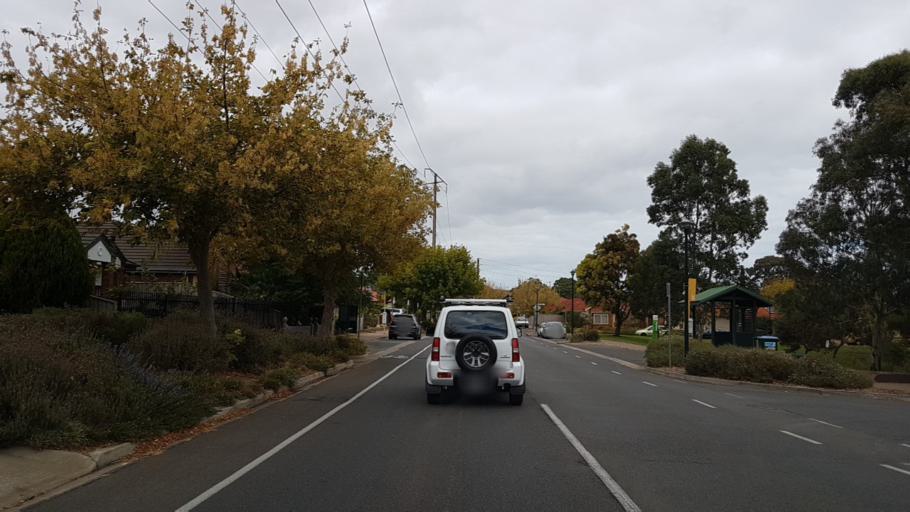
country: AU
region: South Australia
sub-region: Marion
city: Marion
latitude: -35.0150
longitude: 138.5649
